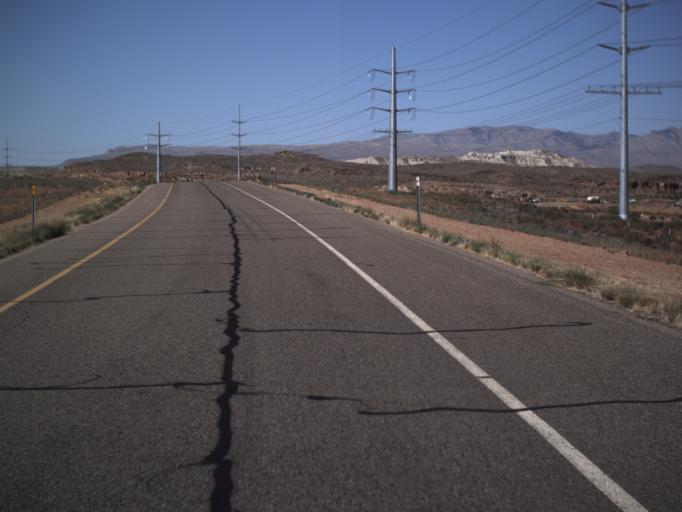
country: US
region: Utah
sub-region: Washington County
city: Saint George
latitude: 37.0100
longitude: -113.5092
